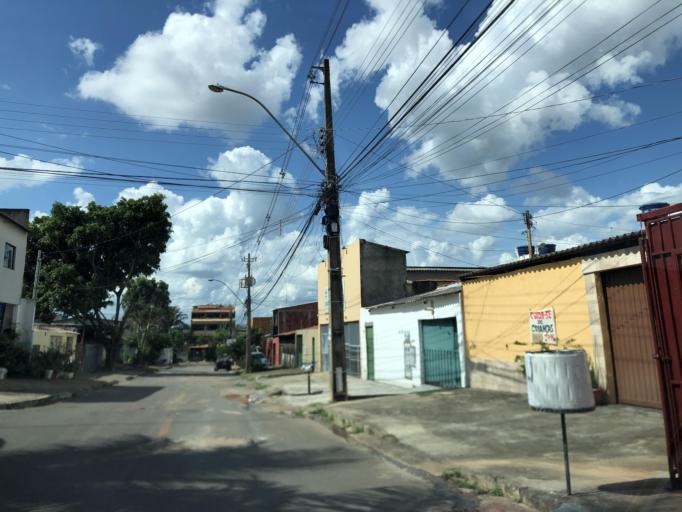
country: BR
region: Federal District
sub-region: Brasilia
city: Brasilia
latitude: -15.8994
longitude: -47.7770
